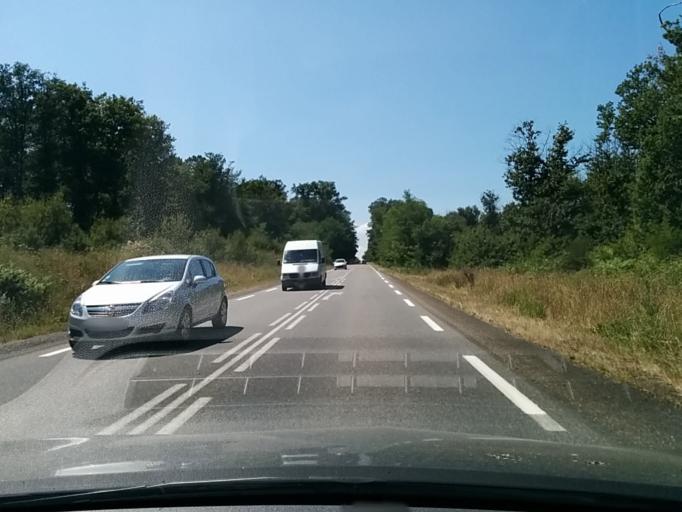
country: FR
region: Aquitaine
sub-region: Departement des Landes
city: Villeneuve-de-Marsan
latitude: 43.8176
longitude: -0.3131
